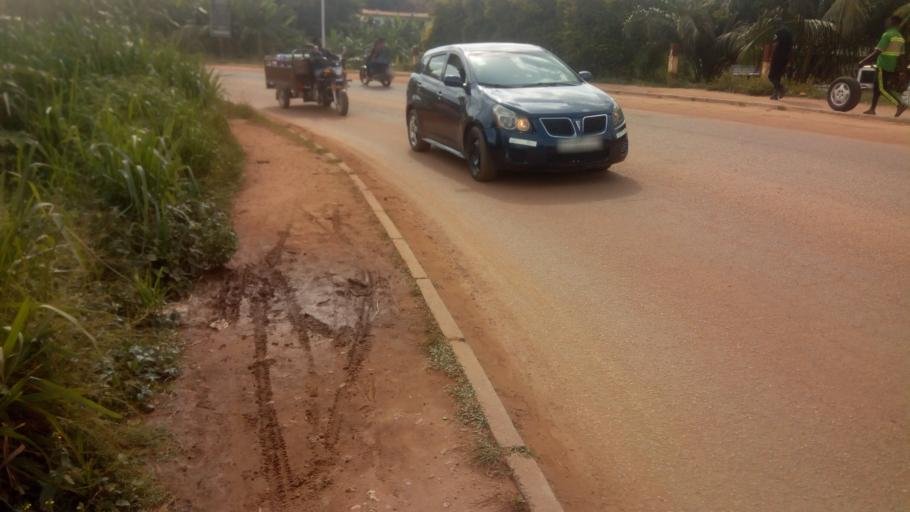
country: GH
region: Ashanti
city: Obuasi
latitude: 6.2115
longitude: -1.6861
